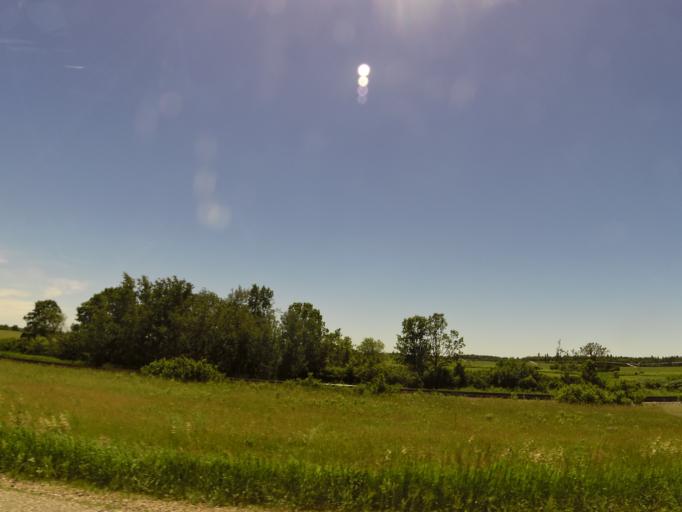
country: US
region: Minnesota
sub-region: Wadena County
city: Wadena
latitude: 46.4594
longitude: -95.1845
